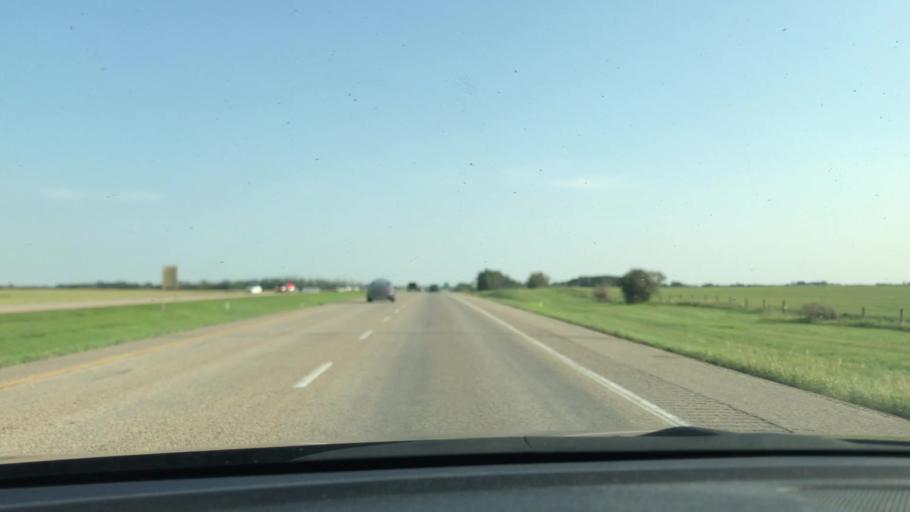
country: CA
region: Alberta
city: Millet
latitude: 53.1074
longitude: -113.5984
